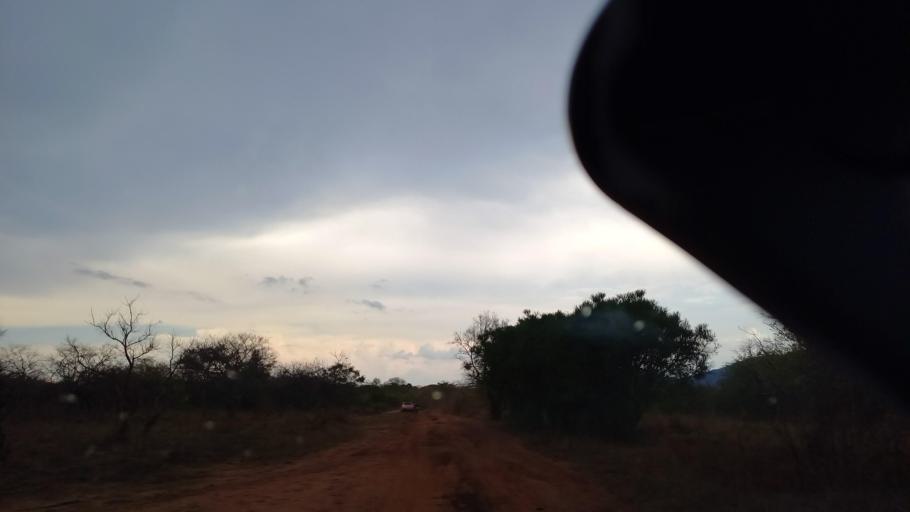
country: ZM
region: Lusaka
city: Kafue
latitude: -15.9995
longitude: 28.2792
